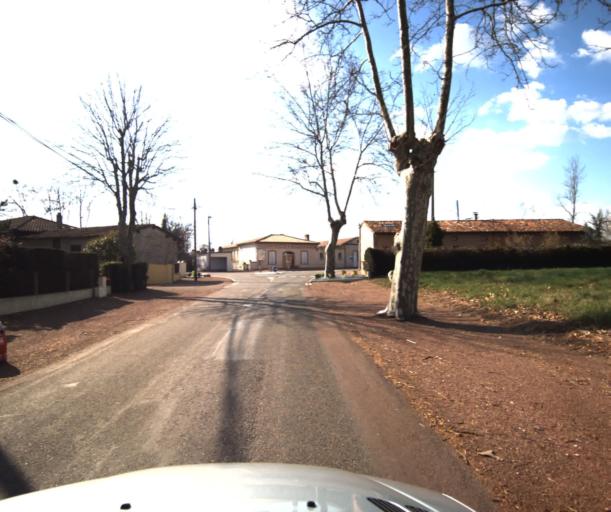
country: FR
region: Midi-Pyrenees
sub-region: Departement du Tarn-et-Garonne
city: Bressols
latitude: 43.9390
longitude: 1.3072
